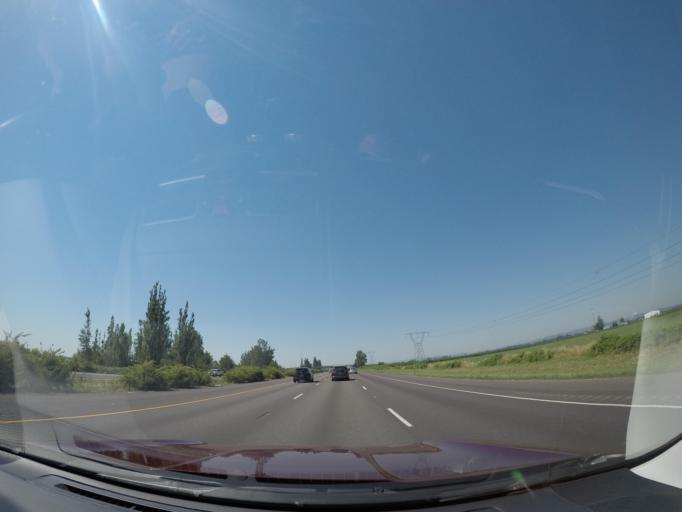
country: US
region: Oregon
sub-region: Marion County
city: Gervais
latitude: 45.0930
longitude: -122.9399
